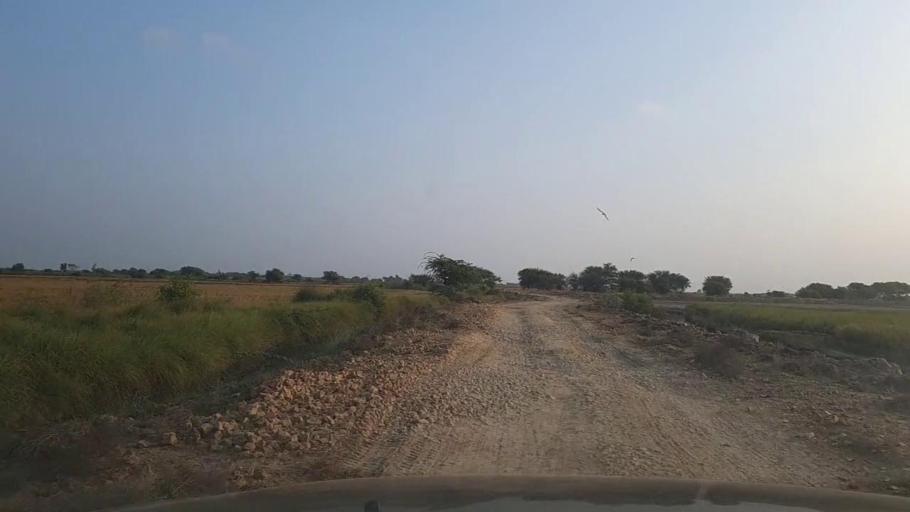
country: PK
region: Sindh
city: Jati
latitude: 24.5386
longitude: 68.3604
